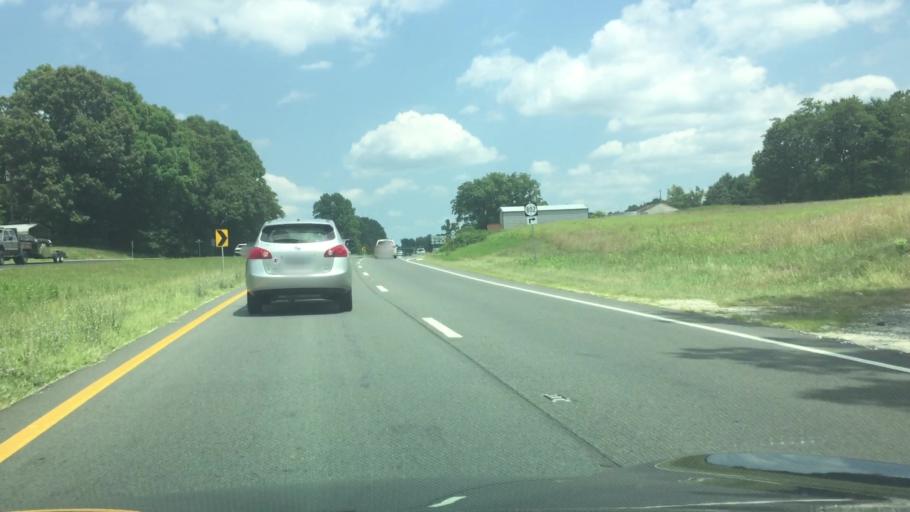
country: US
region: Virginia
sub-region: Campbell County
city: Concord
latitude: 37.3514
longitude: -78.9835
